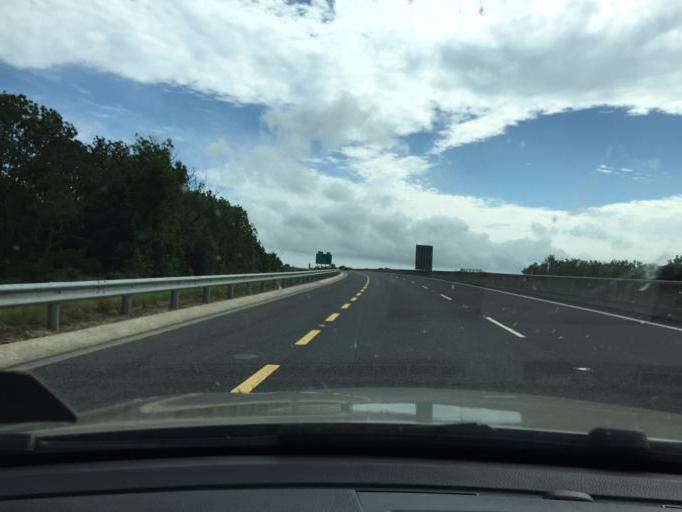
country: IE
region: Leinster
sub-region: Kilkenny
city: Mooncoin
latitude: 52.2536
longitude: -7.1902
